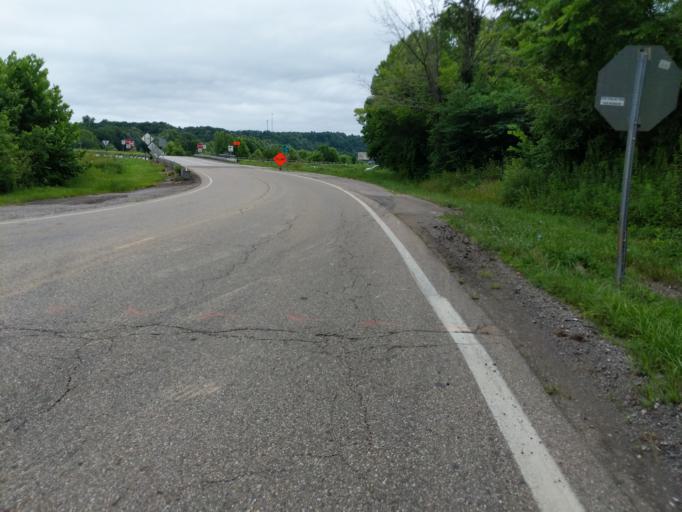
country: US
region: Ohio
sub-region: Athens County
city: Chauncey
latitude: 39.3906
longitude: -82.1436
